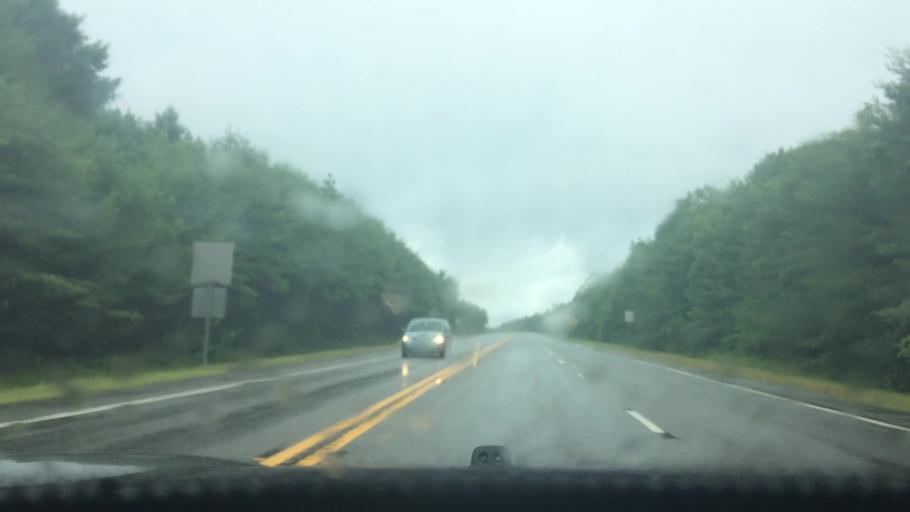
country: US
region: Massachusetts
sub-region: Worcester County
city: South Ashburnham
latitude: 42.5926
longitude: -71.9622
